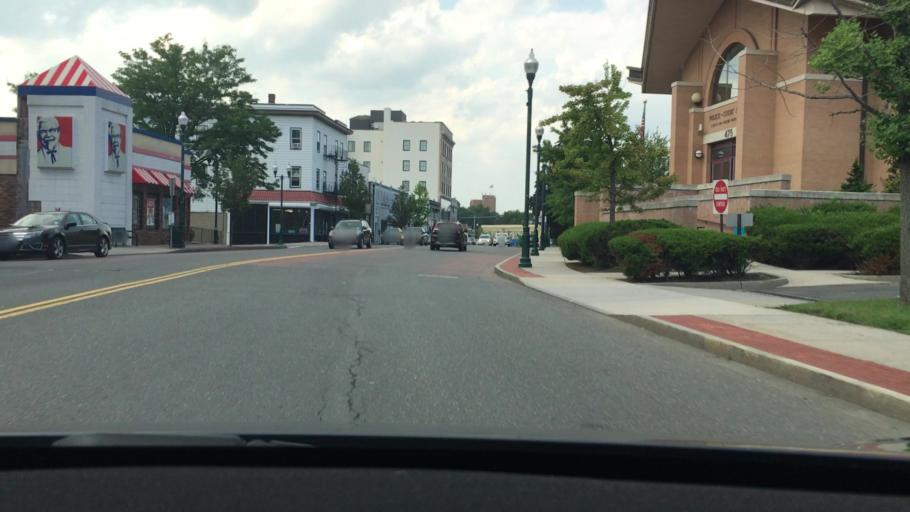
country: US
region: New York
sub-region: Westchester County
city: New Rochelle
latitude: 40.9187
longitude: -73.7864
